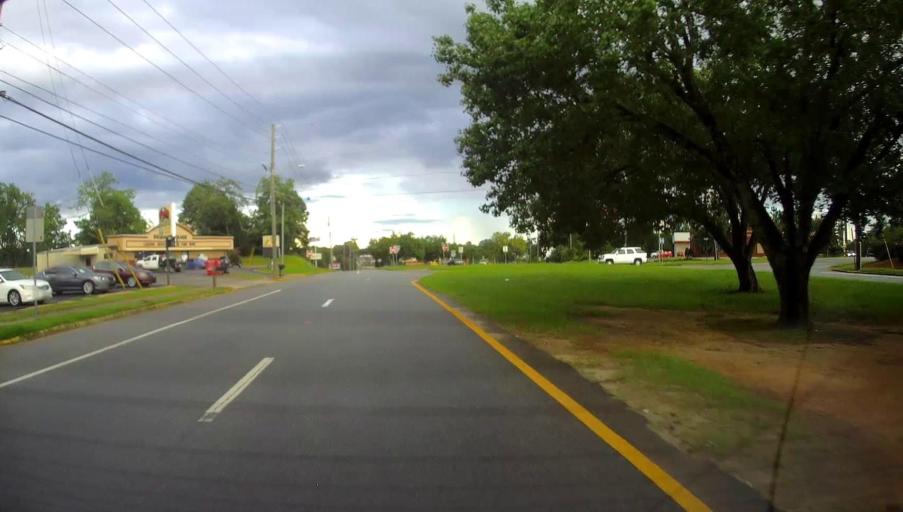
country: US
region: Georgia
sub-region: Houston County
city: Perry
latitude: 32.4664
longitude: -83.7385
